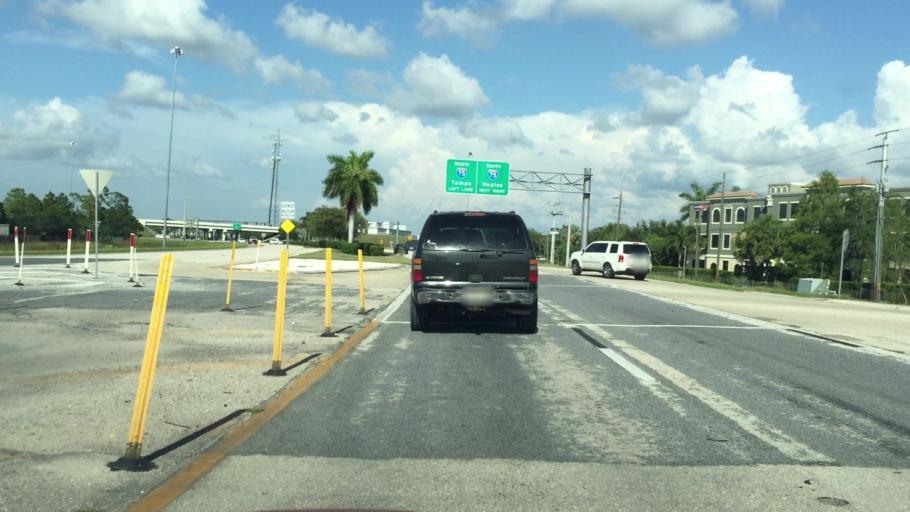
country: US
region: Florida
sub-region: Lee County
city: Estero
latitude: 26.4312
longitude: -81.7820
